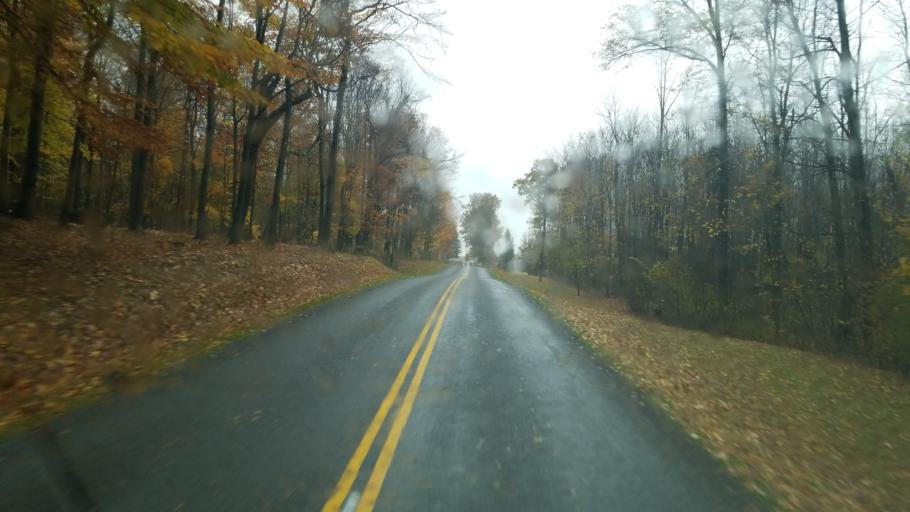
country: US
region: Ohio
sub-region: Richland County
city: Ontario
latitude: 40.7430
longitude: -82.6084
